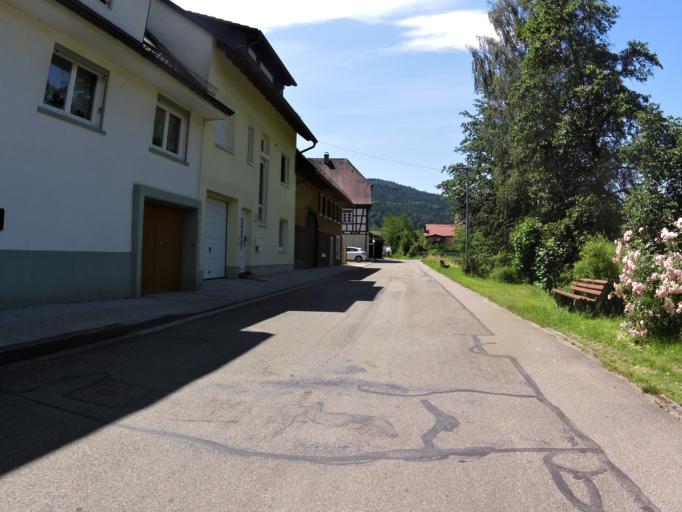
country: DE
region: Baden-Wuerttemberg
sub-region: Freiburg Region
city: Seelbach
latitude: 48.3048
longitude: 7.9384
